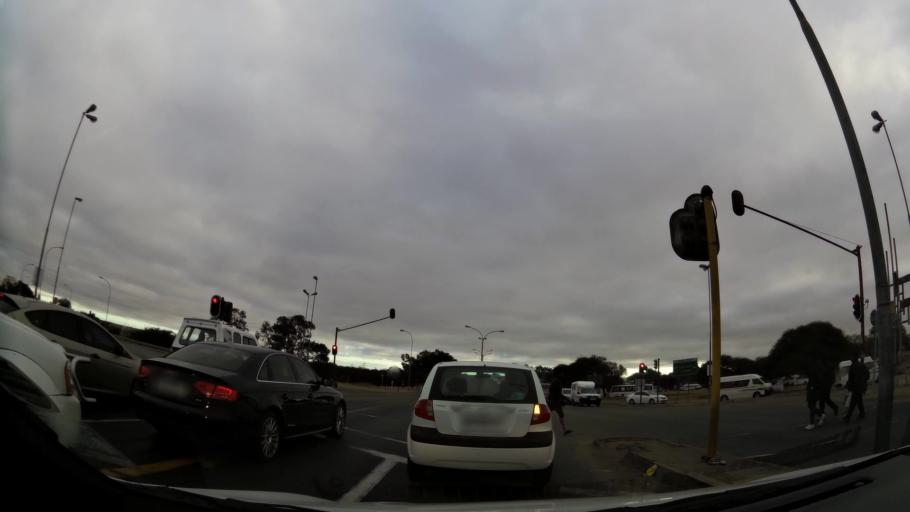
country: ZA
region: Limpopo
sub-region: Capricorn District Municipality
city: Polokwane
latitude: -23.9045
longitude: 29.4417
